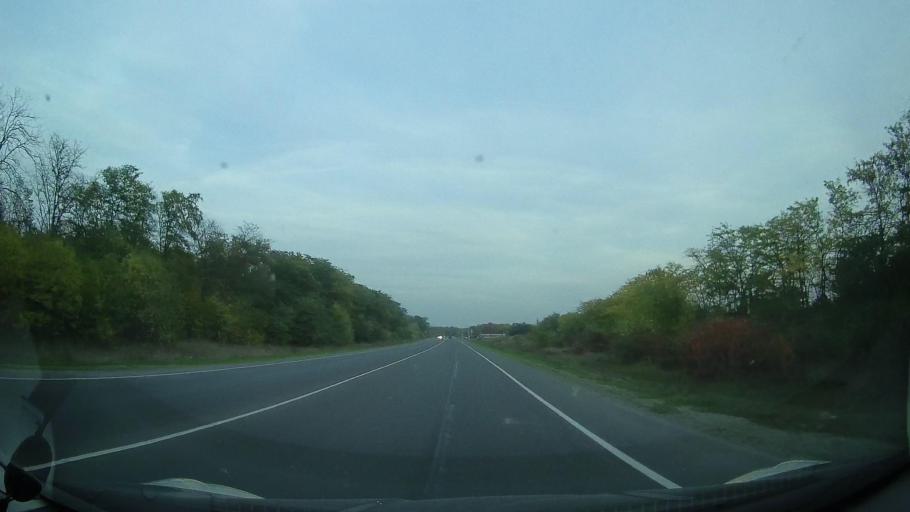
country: RU
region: Rostov
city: Kirovskaya
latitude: 46.9973
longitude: 39.9989
